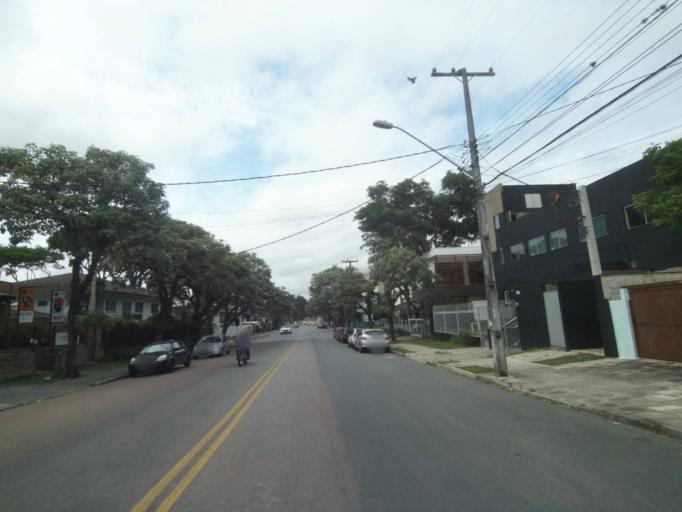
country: BR
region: Parana
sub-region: Curitiba
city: Curitiba
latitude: -25.4156
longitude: -49.2478
